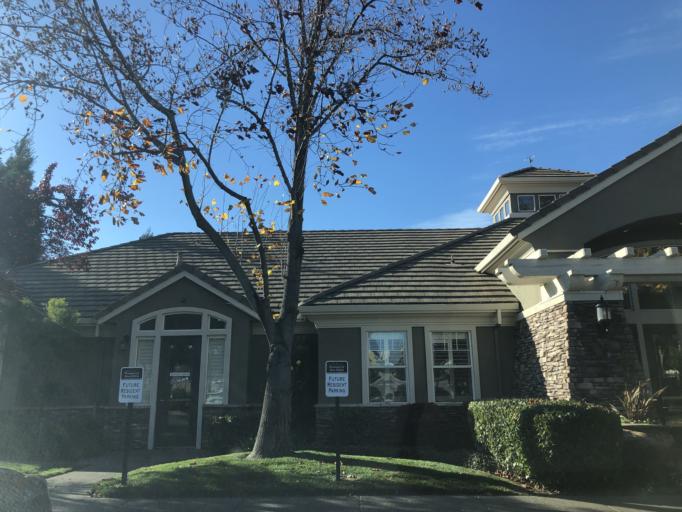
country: US
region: California
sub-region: Placer County
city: Roseville
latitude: 38.7719
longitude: -121.2740
